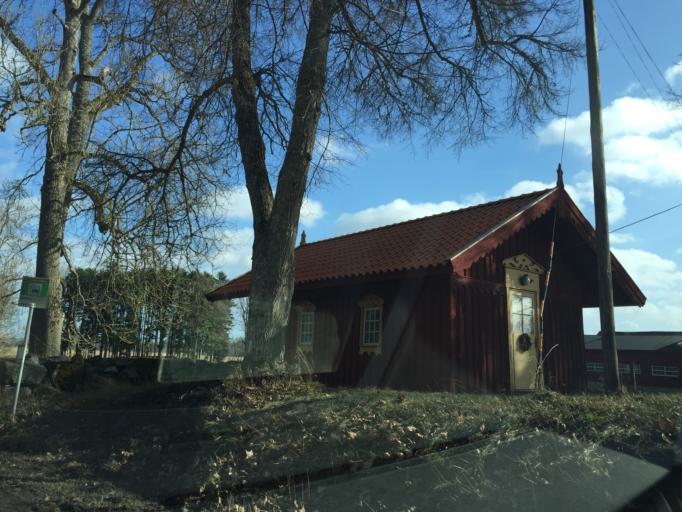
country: SE
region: Soedermanland
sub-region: Vingakers Kommun
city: Vingaker
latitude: 59.0368
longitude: 15.7169
